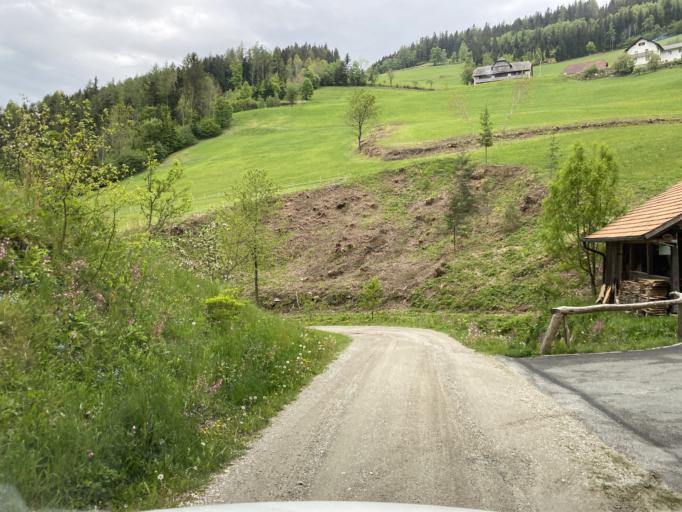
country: AT
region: Styria
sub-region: Politischer Bezirk Weiz
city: Birkfeld
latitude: 47.3334
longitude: 15.6587
